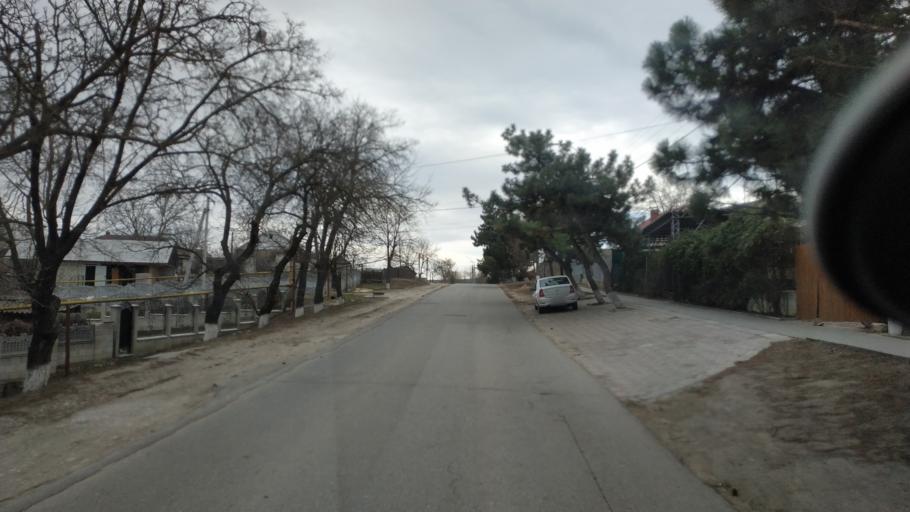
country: MD
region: Chisinau
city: Vadul lui Voda
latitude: 47.0960
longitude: 29.0714
